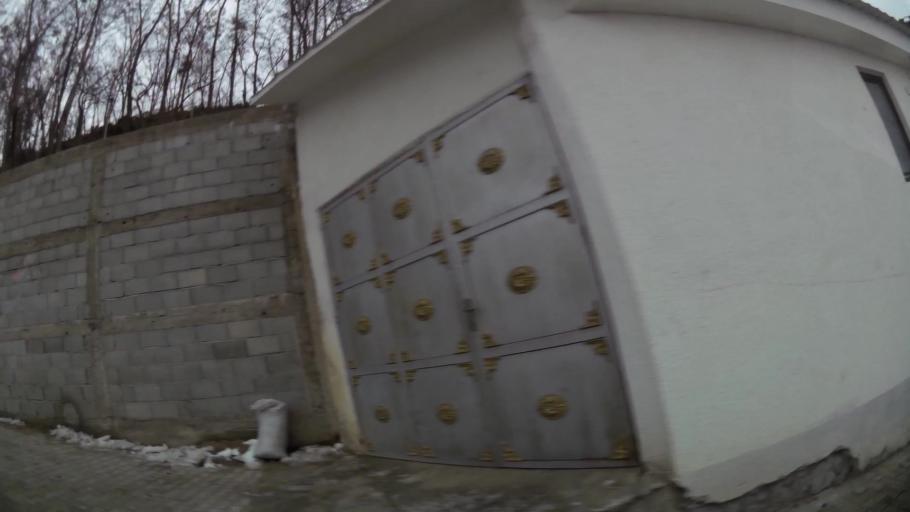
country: MK
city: Kondovo
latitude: 42.0118
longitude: 21.3165
